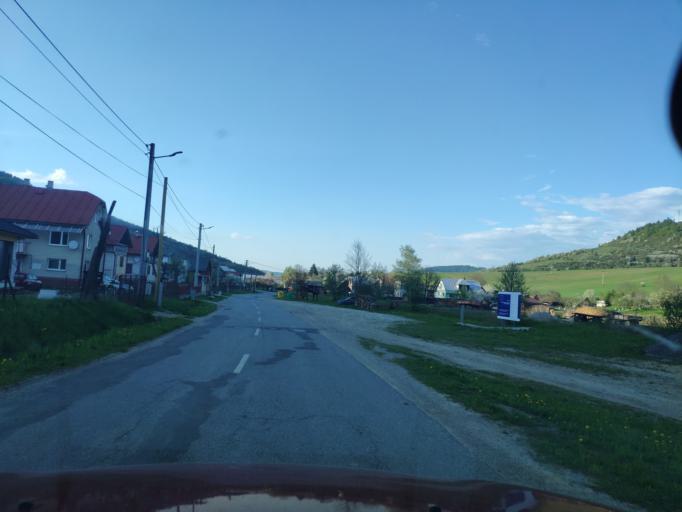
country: SK
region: Presovsky
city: Lipany
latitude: 49.0947
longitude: 20.8486
